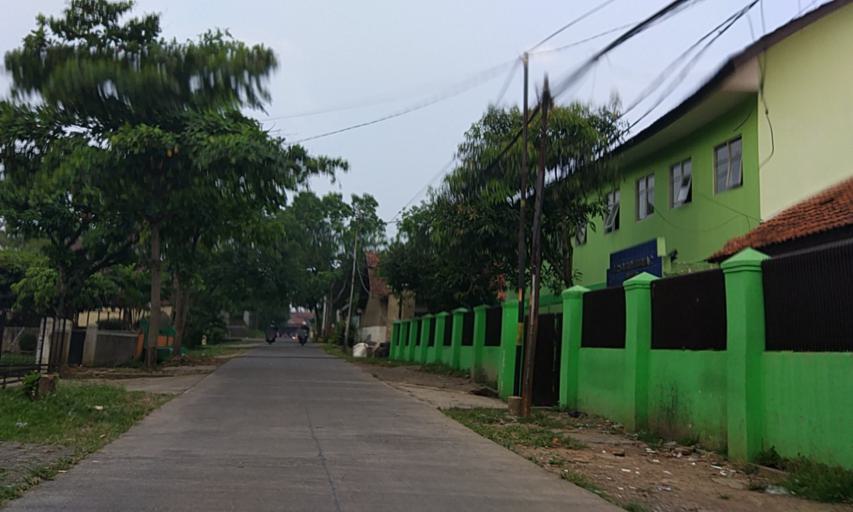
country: ID
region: West Java
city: Bandung
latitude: -6.9072
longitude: 107.6756
